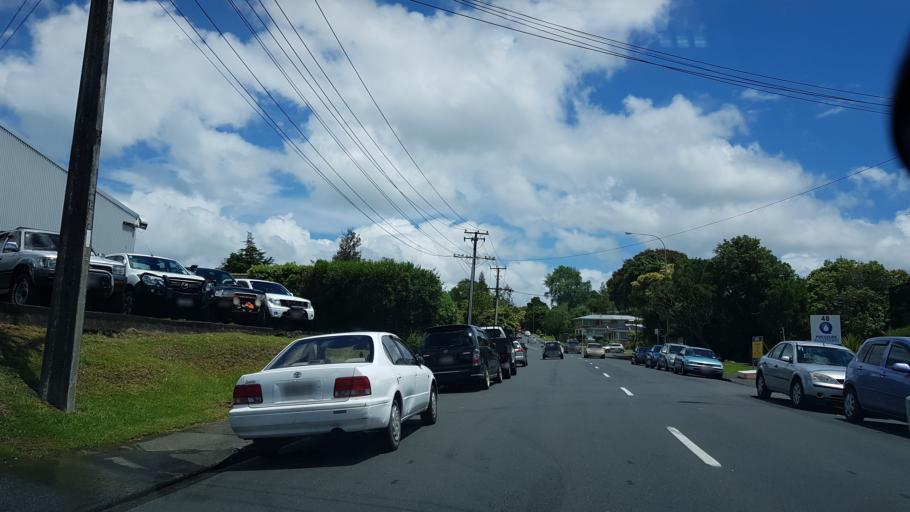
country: NZ
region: Auckland
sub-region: Auckland
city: North Shore
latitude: -36.7756
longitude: 174.7327
